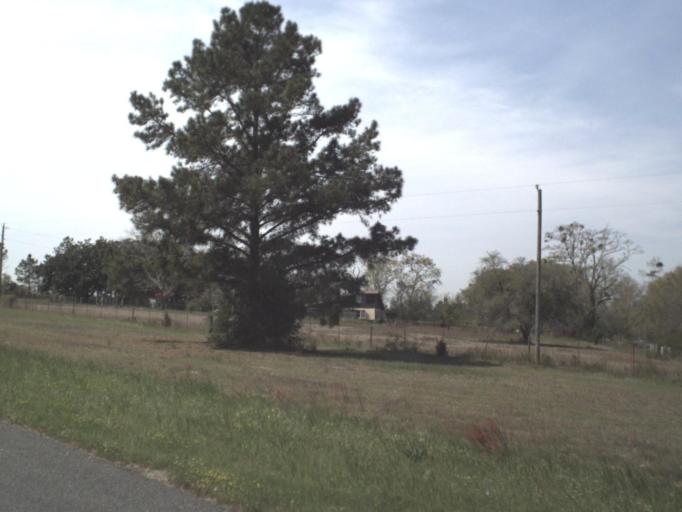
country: US
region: Florida
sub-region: Walton County
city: DeFuniak Springs
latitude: 30.7256
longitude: -85.9759
